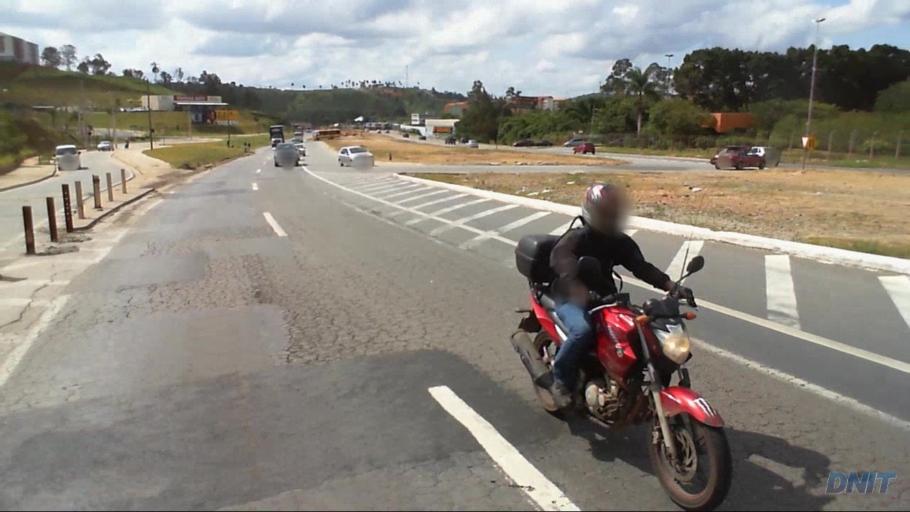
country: BR
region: Minas Gerais
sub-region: Santa Luzia
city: Santa Luzia
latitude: -19.8460
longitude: -43.8874
